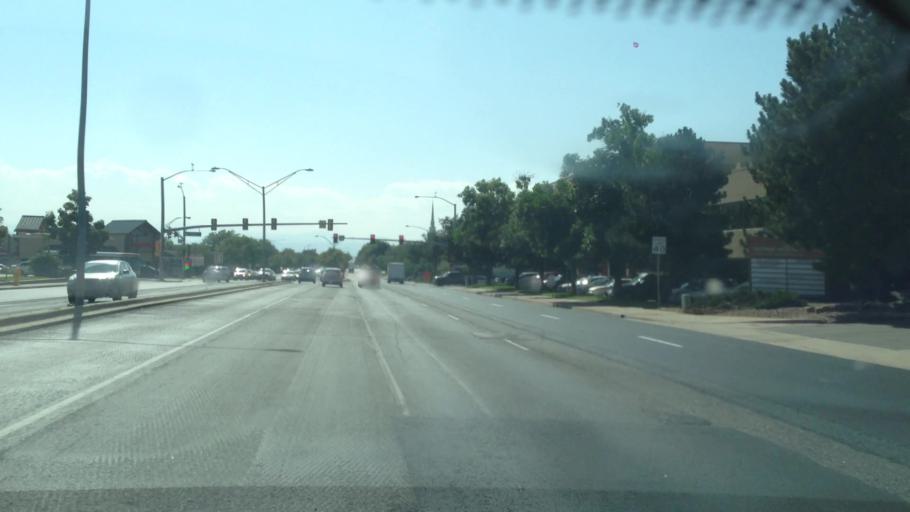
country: US
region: Colorado
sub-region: Adams County
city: Aurora
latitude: 39.6966
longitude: -104.8318
